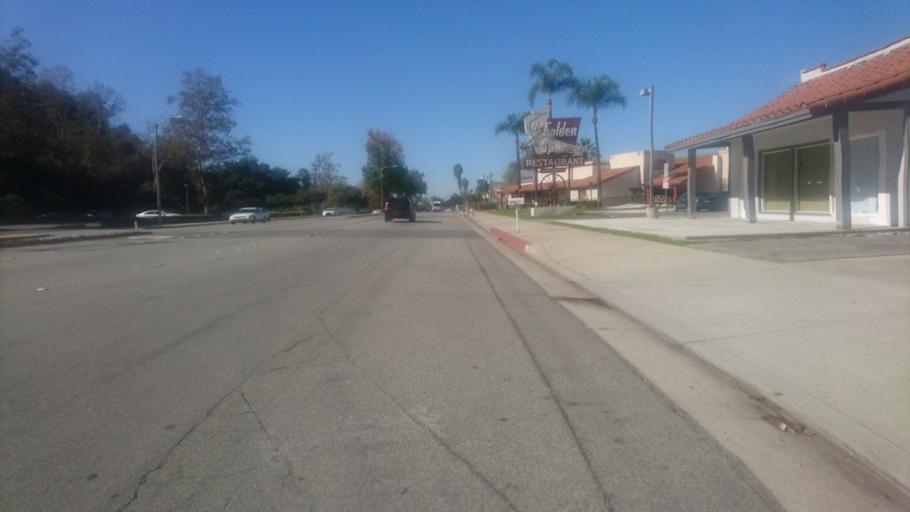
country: US
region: California
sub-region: Los Angeles County
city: Glendora
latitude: 34.1289
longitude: -117.8426
